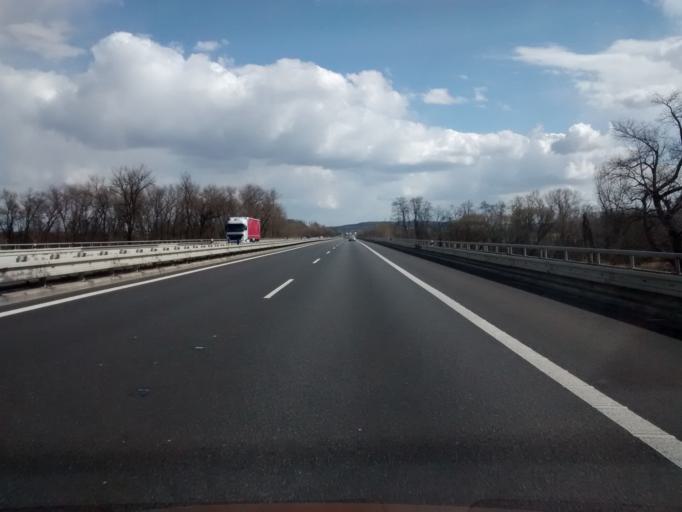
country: CZ
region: Central Bohemia
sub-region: Okres Melnik
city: Veltrusy
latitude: 50.3059
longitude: 14.3239
